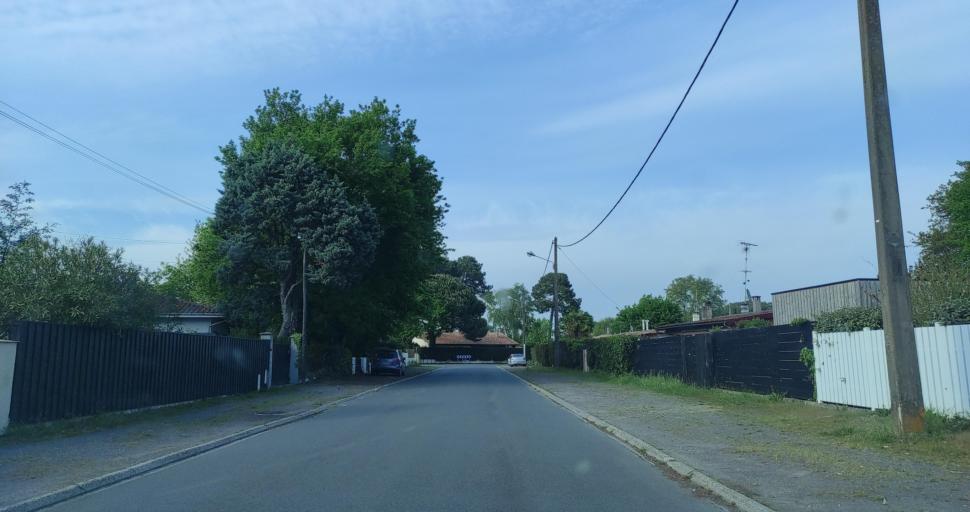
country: FR
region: Aquitaine
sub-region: Departement de la Gironde
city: Ares
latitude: 44.7633
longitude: -1.1281
